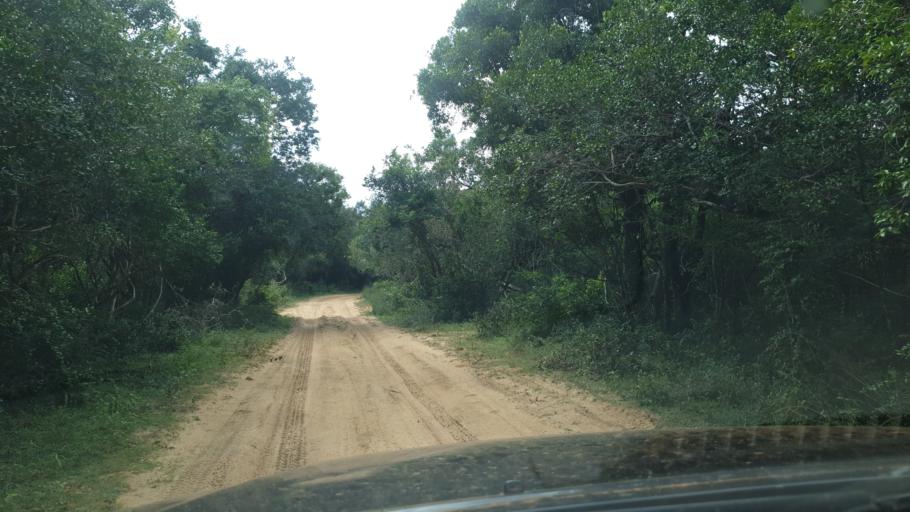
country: LK
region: North Central
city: Anuradhapura
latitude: 8.4185
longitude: 80.0088
